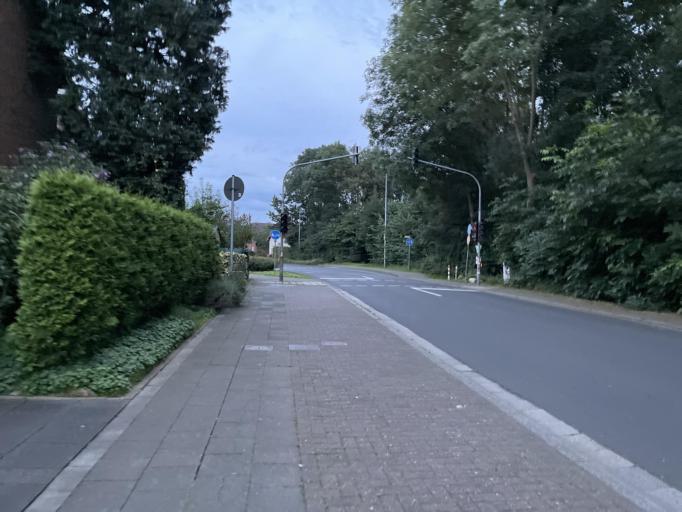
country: DE
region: North Rhine-Westphalia
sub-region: Regierungsbezirk Koln
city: Bergheim
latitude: 50.9450
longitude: 6.6460
